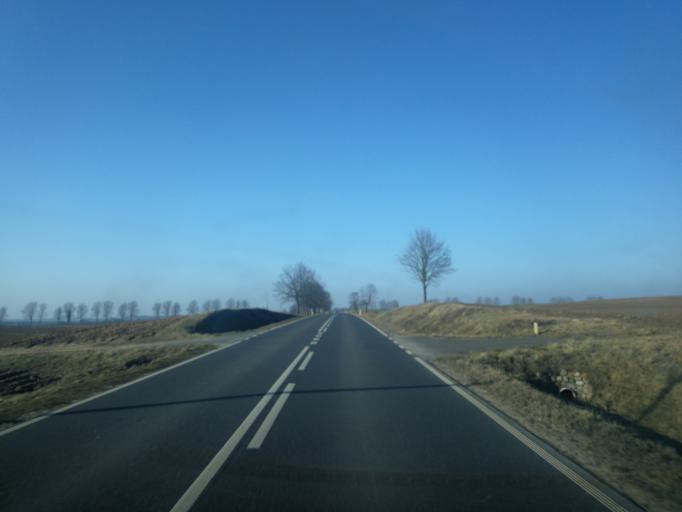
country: PL
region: Warmian-Masurian Voivodeship
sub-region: Powiat ilawski
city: Lubawa
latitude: 53.4136
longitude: 19.7921
